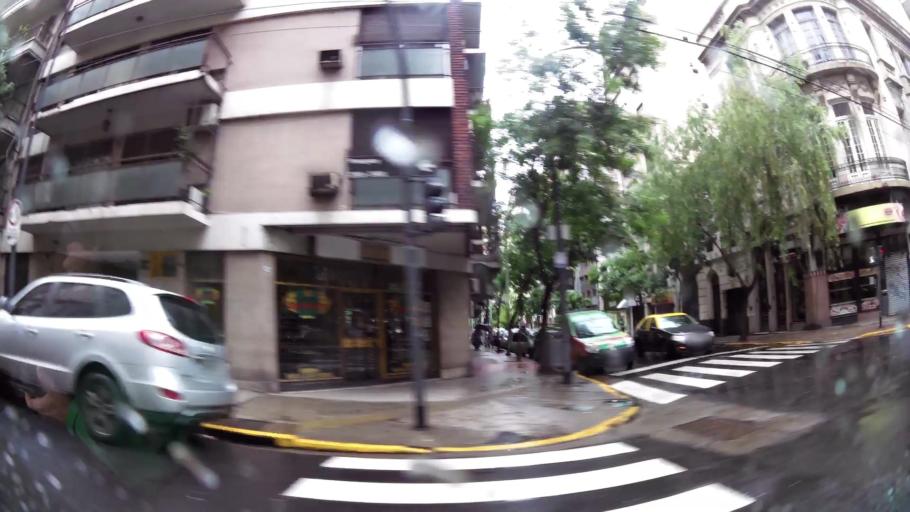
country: AR
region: Buenos Aires F.D.
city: Retiro
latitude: -34.5978
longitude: -58.4020
